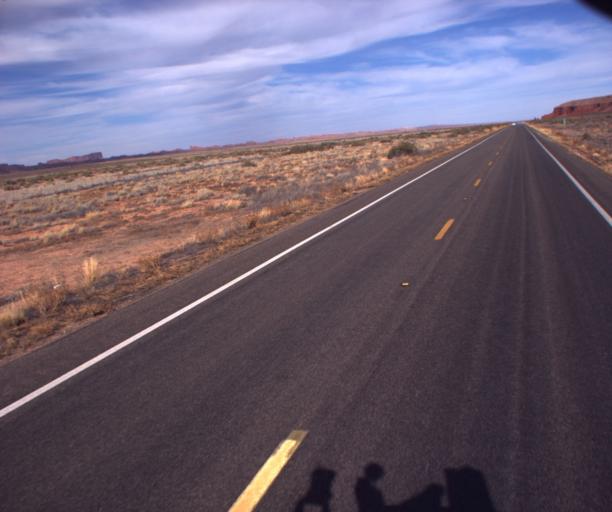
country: US
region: Arizona
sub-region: Navajo County
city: Kayenta
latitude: 36.7552
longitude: -110.0538
